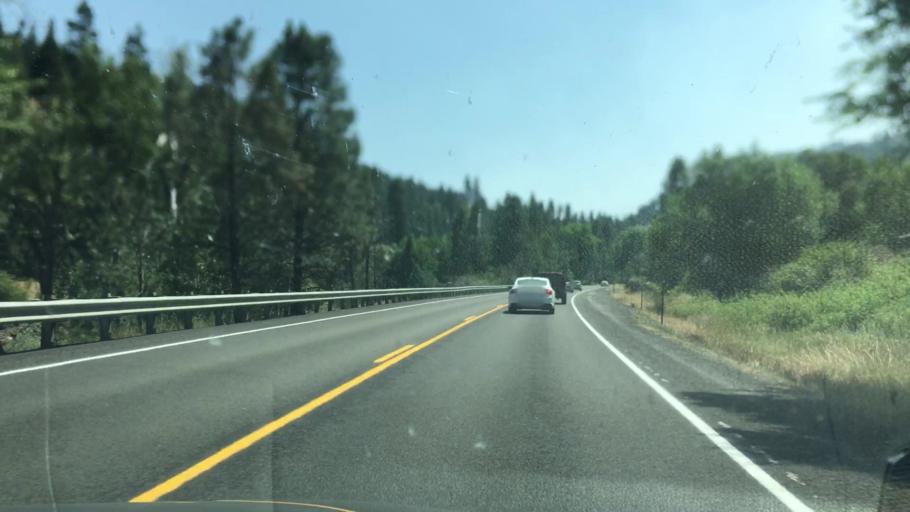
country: US
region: Idaho
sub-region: Valley County
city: McCall
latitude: 45.2493
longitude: -116.3329
